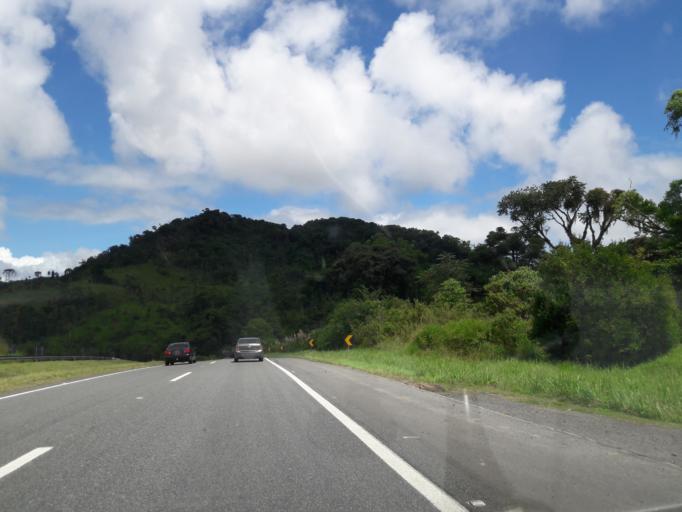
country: BR
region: Parana
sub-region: Antonina
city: Antonina
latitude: -25.0191
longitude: -48.5134
